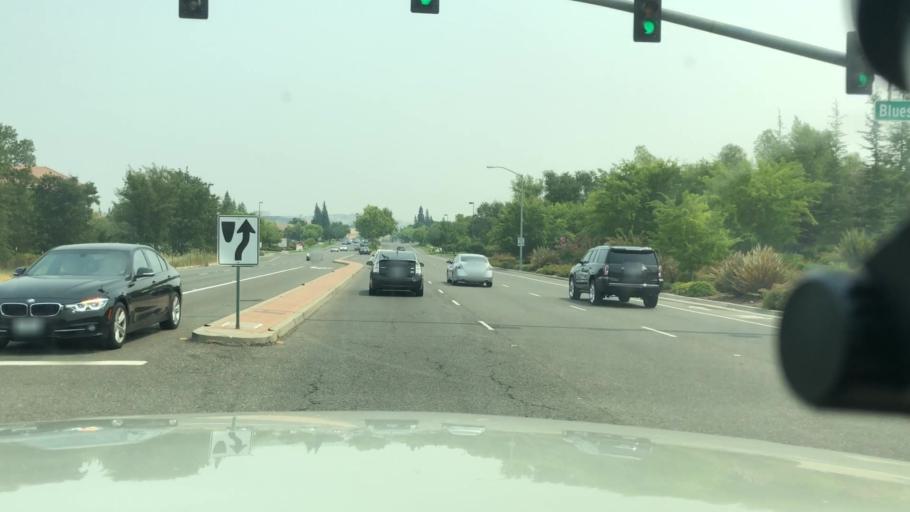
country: US
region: California
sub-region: Sacramento County
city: Folsom
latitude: 38.6666
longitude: -121.1435
